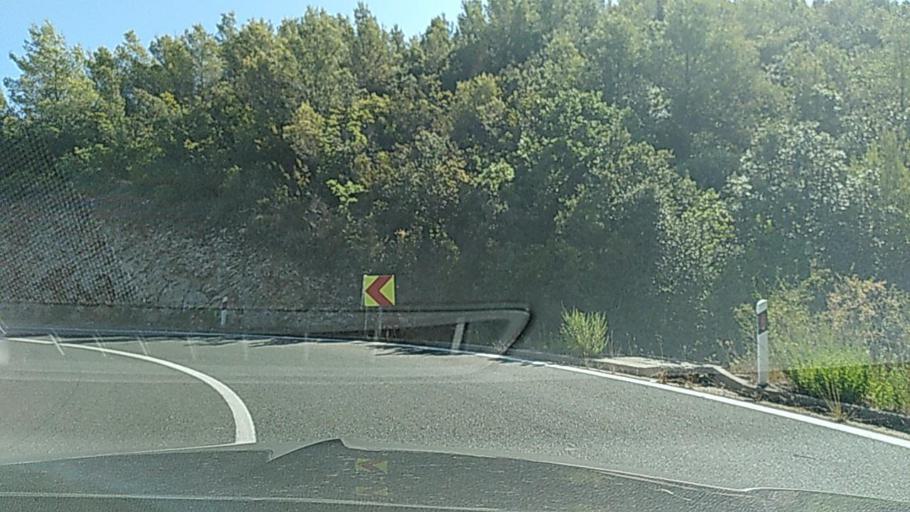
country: HR
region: Splitsko-Dalmatinska
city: Jelsa
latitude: 43.1434
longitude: 16.7747
